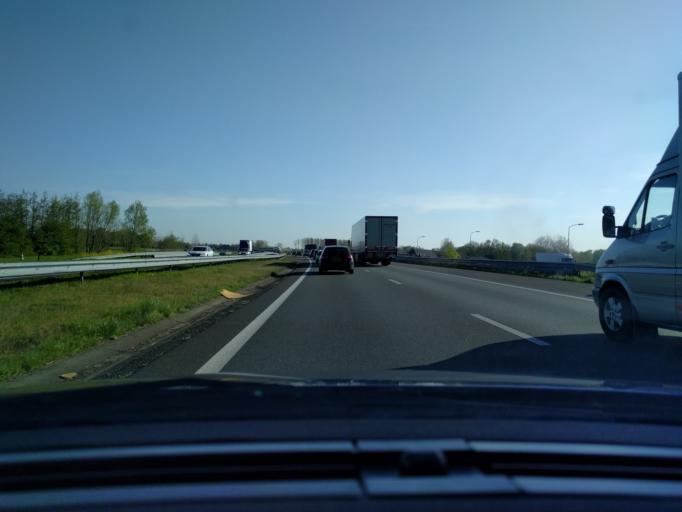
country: NL
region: North Brabant
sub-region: Gemeente Sint-Oedenrode
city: Sint-Oedenrode
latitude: 51.5660
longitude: 5.4746
